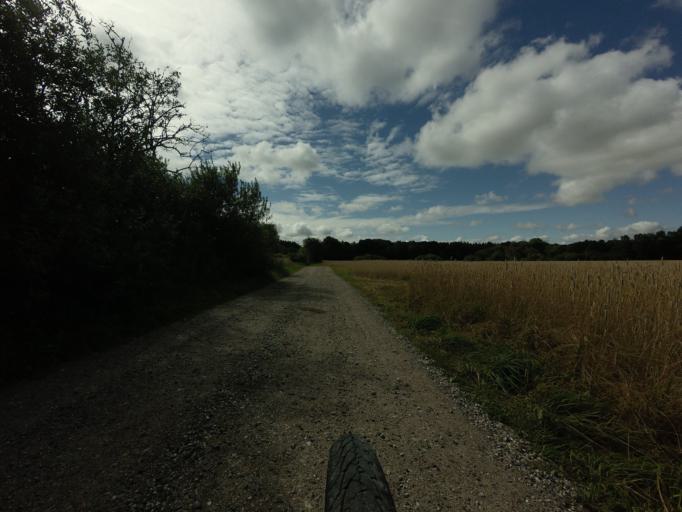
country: DK
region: Central Jutland
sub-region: Norddjurs Kommune
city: Auning
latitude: 56.4389
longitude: 10.3654
